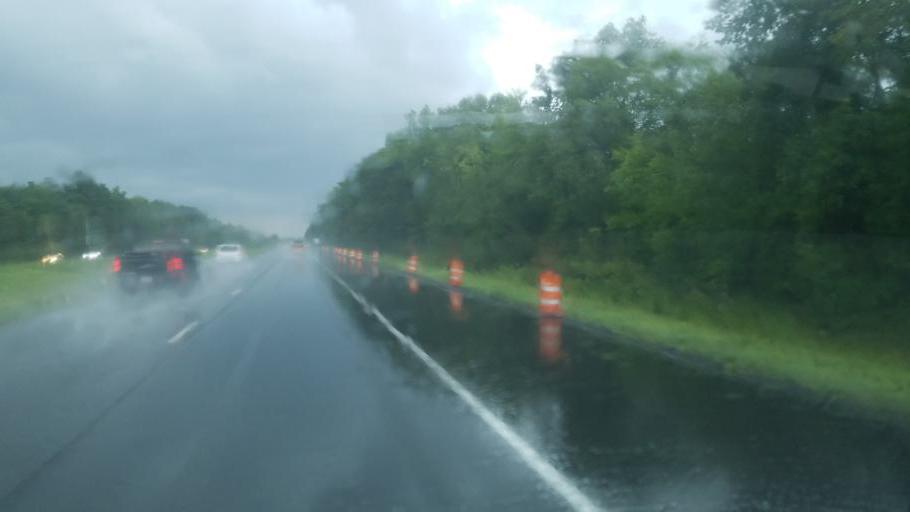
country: US
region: Ohio
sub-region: Trumbull County
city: Churchill
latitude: 41.1773
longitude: -80.6852
